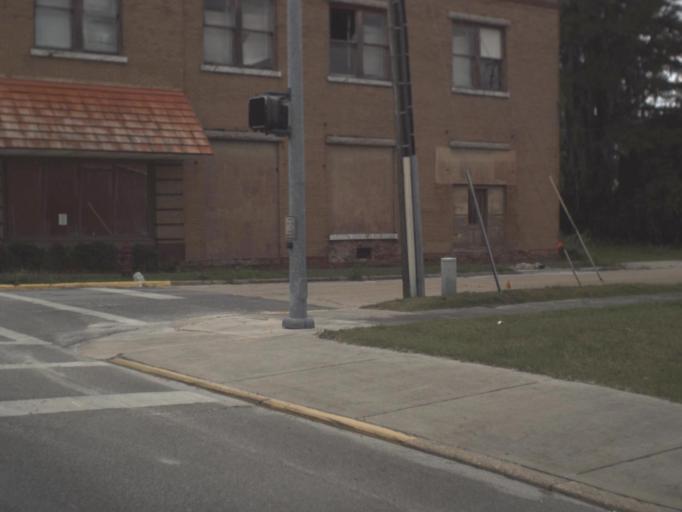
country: US
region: Florida
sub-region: Hamilton County
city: Jasper
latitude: 30.5183
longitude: -82.9486
